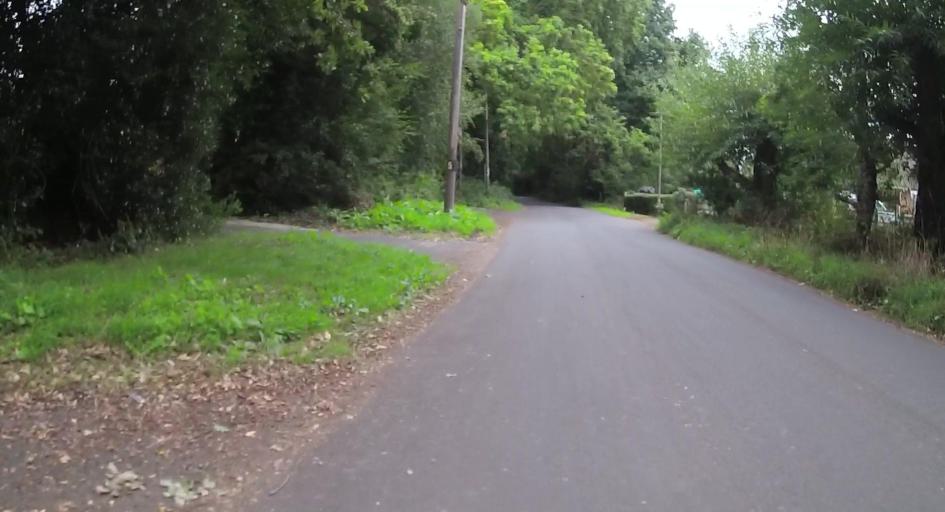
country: GB
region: England
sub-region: Surrey
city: Windlesham
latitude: 51.3373
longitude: -0.6504
